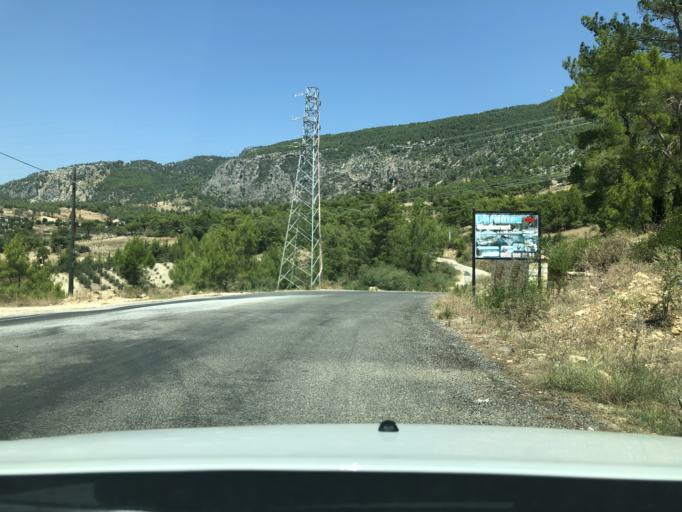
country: TR
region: Antalya
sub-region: Manavgat
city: Manavgat
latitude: 36.8759
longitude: 31.5498
